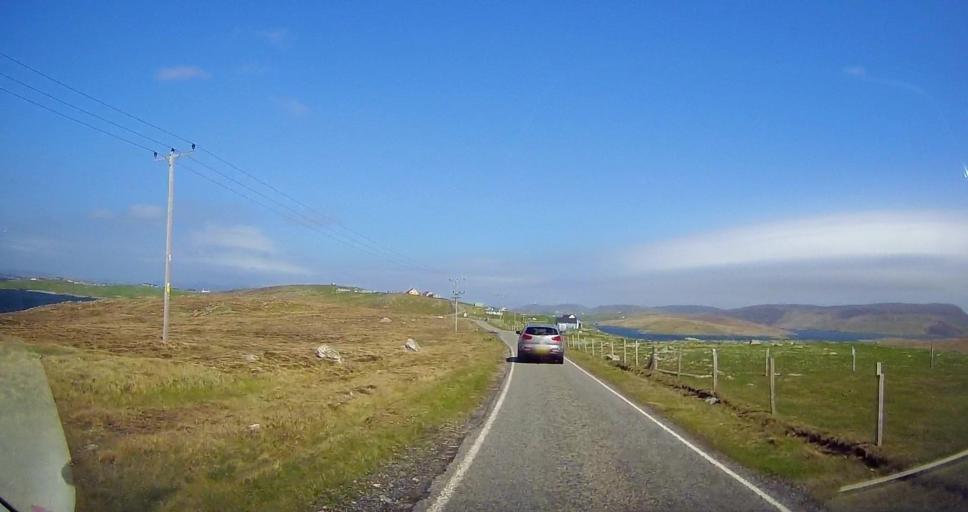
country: GB
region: Scotland
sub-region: Shetland Islands
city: Sandwick
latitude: 60.0897
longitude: -1.3270
